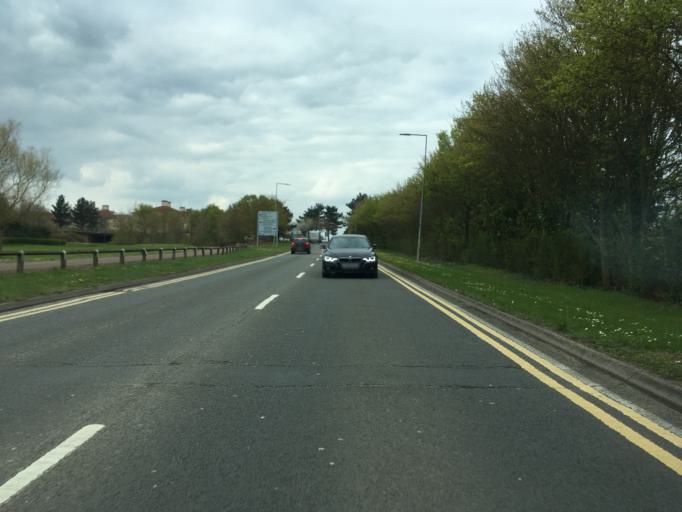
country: GB
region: England
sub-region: Milton Keynes
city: Milton Keynes
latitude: 52.0529
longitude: -0.7274
